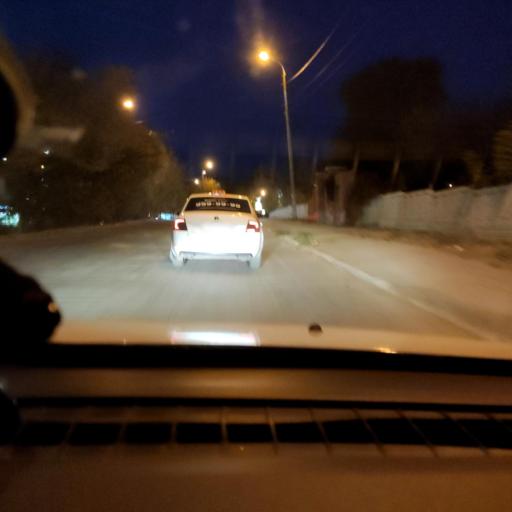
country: RU
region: Samara
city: Samara
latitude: 53.1952
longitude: 50.1579
